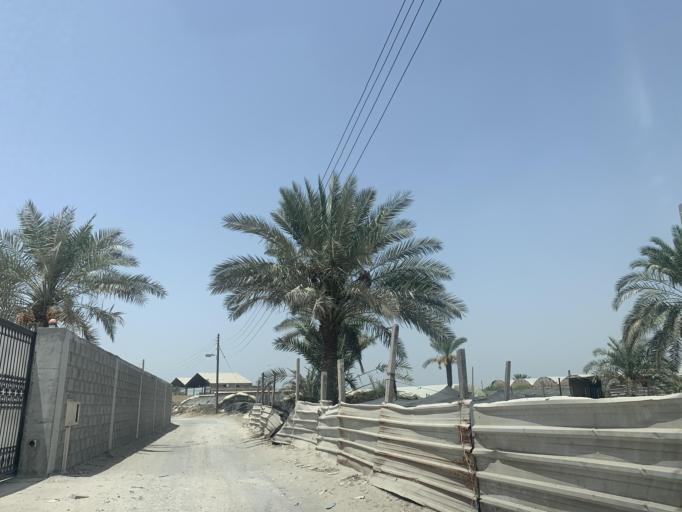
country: BH
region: Central Governorate
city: Madinat Hamad
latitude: 26.1537
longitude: 50.4970
